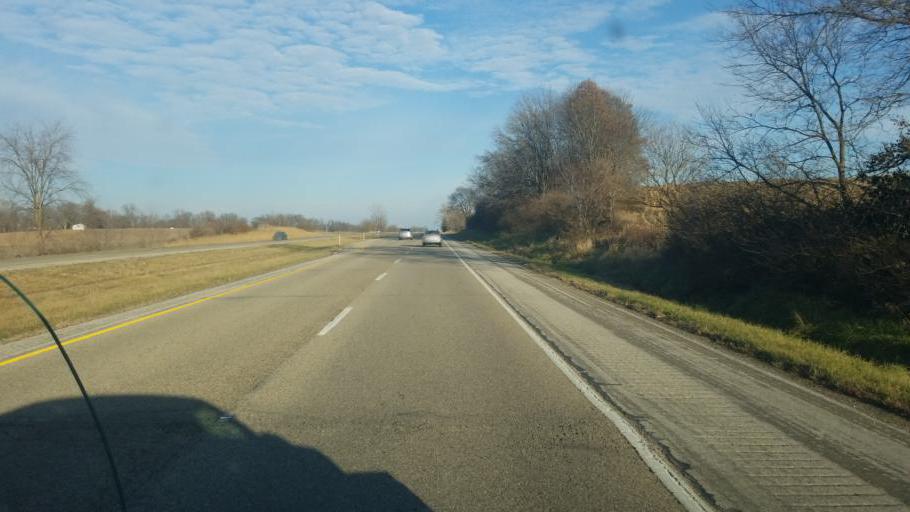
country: US
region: Indiana
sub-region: Knox County
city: Vincennes
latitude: 38.6766
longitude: -87.4232
